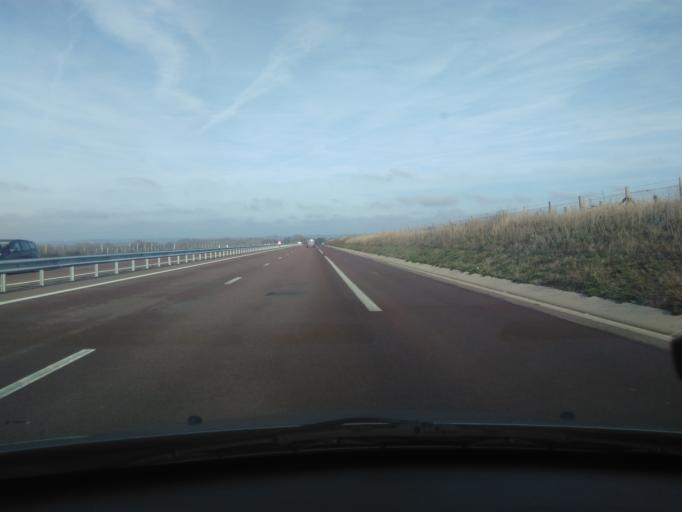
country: FR
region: Bourgogne
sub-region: Departement de la Nievre
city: Saint-Pierre-le-Moutier
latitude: 46.8279
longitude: 3.1255
